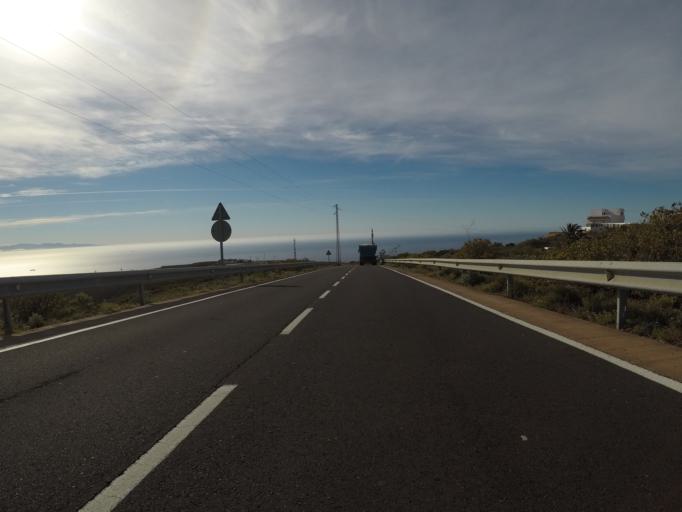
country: ES
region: Canary Islands
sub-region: Provincia de Santa Cruz de Tenerife
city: Lomo de Arico
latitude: 28.1645
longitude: -16.4986
